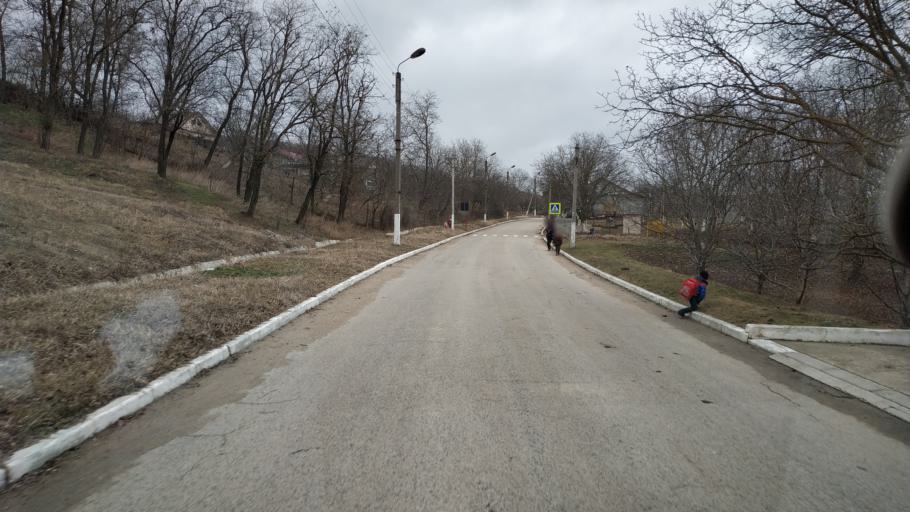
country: MD
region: Calarasi
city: Calarasi
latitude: 47.2654
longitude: 28.3532
